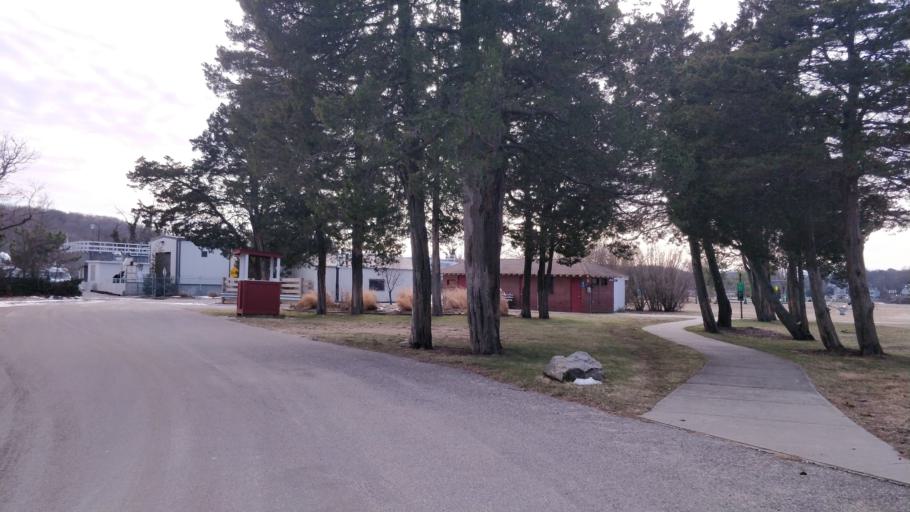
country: US
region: New York
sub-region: Suffolk County
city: Northport
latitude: 40.8937
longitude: -73.3552
